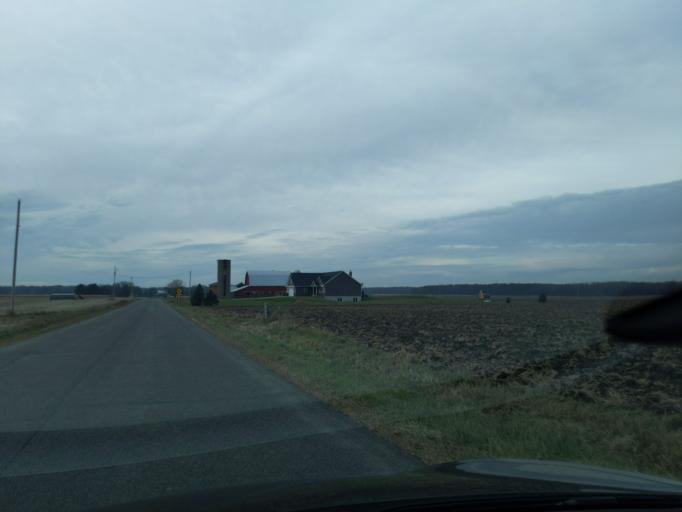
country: US
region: Michigan
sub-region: Ingham County
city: Okemos
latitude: 42.6546
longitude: -84.3797
